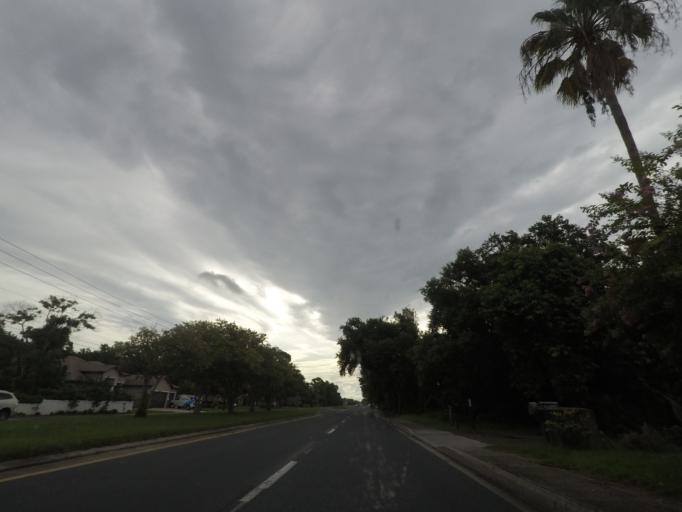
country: US
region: Florida
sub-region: Pinellas County
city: Redington Shores
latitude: 27.8437
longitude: -82.8268
